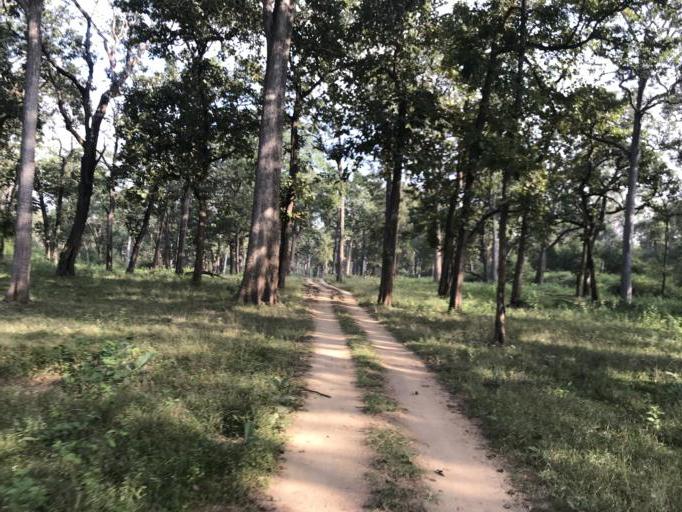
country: IN
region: Karnataka
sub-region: Mysore
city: Heggadadevankote
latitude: 11.9638
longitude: 76.2035
